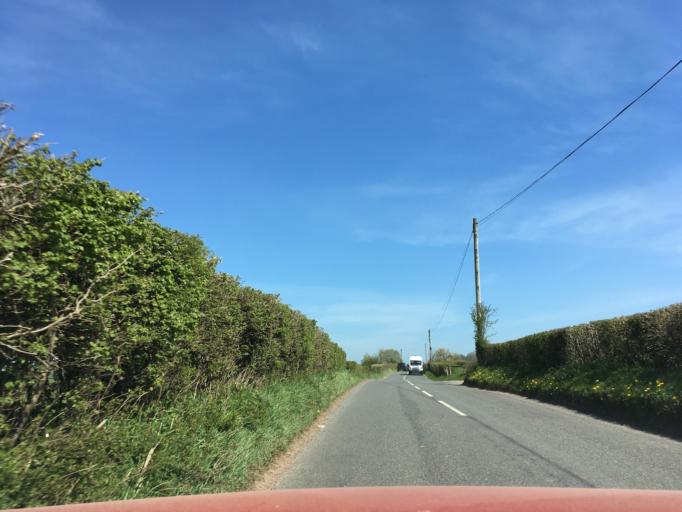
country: GB
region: Wales
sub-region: Monmouthshire
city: Llangwm
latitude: 51.7214
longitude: -2.8386
